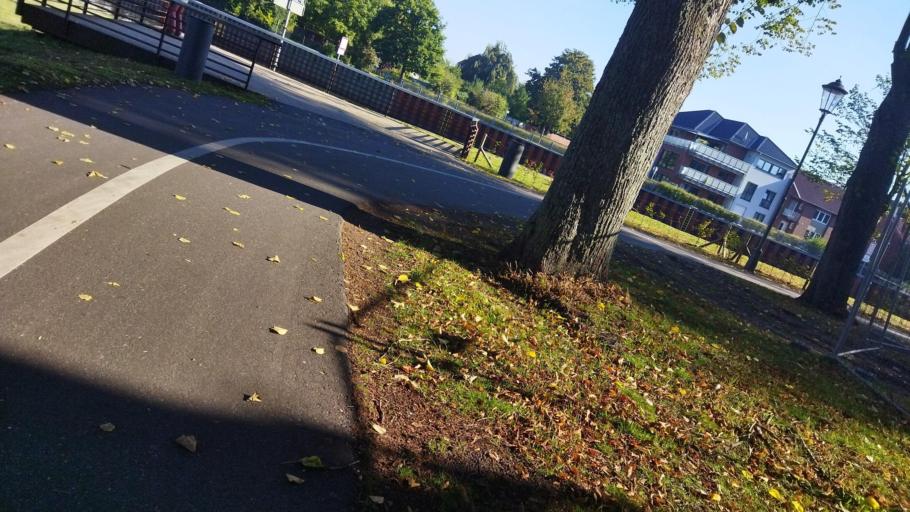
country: DE
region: Lower Saxony
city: Meppen
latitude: 52.6946
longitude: 7.2908
